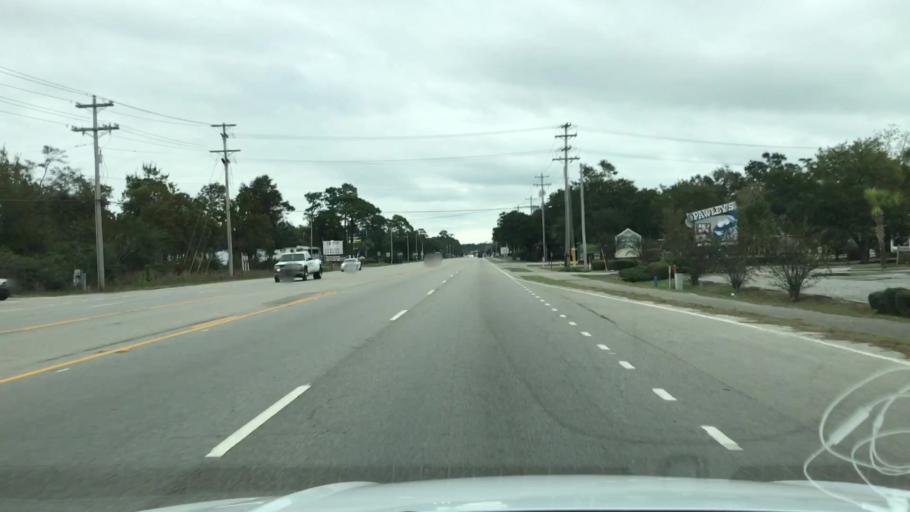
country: US
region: South Carolina
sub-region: Georgetown County
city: Murrells Inlet
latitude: 33.4311
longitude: -79.1432
